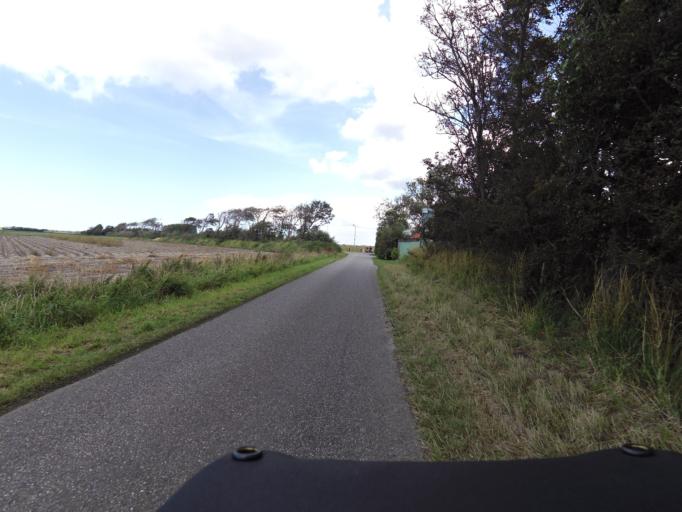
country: NL
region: South Holland
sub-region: Gemeente Goeree-Overflakkee
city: Ouddorp
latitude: 51.8038
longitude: 3.8854
